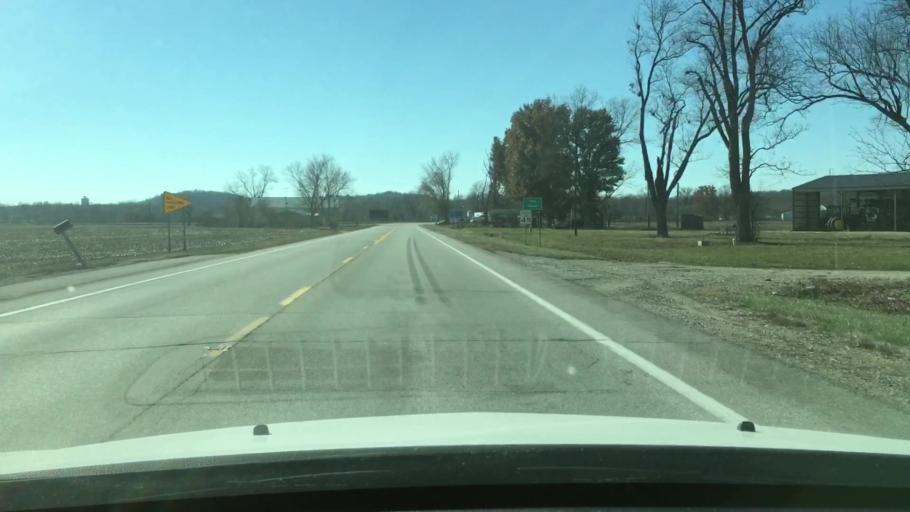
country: US
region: Missouri
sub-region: Pike County
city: Louisiana
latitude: 39.4649
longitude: -91.0290
